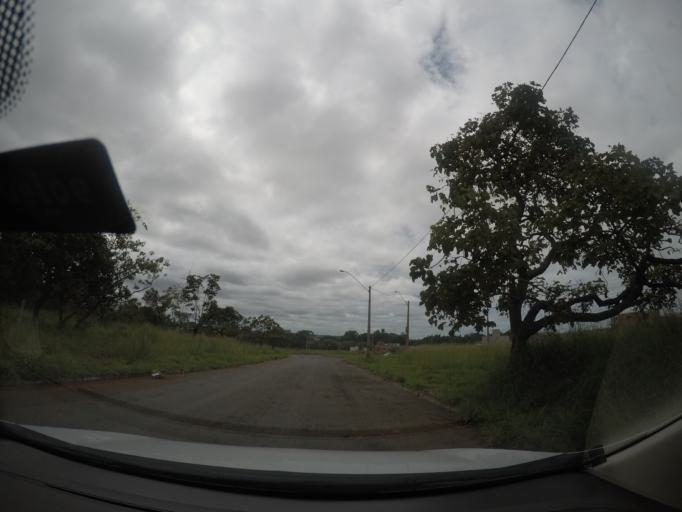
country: BR
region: Goias
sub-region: Goiania
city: Goiania
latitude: -16.7430
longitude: -49.3811
